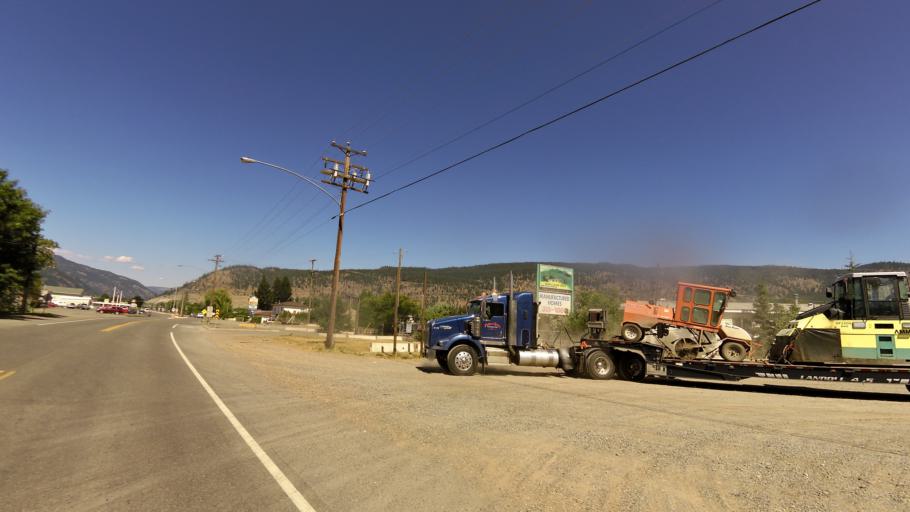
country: CA
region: British Columbia
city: Merritt
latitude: 50.1091
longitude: -120.7783
